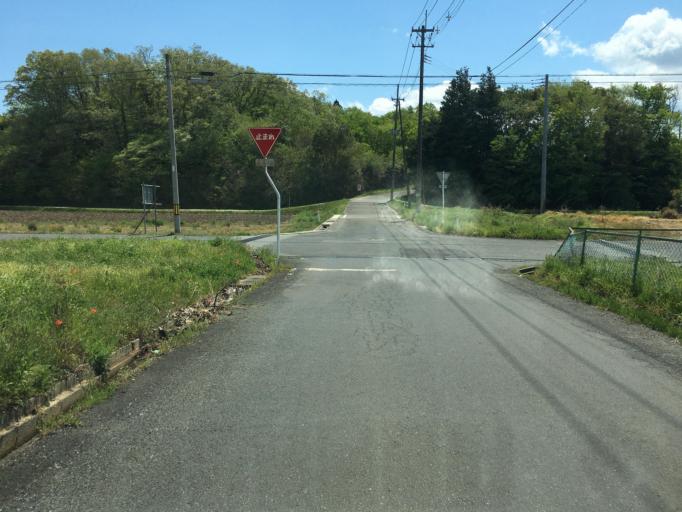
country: JP
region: Miyagi
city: Marumori
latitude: 37.8115
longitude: 140.9488
